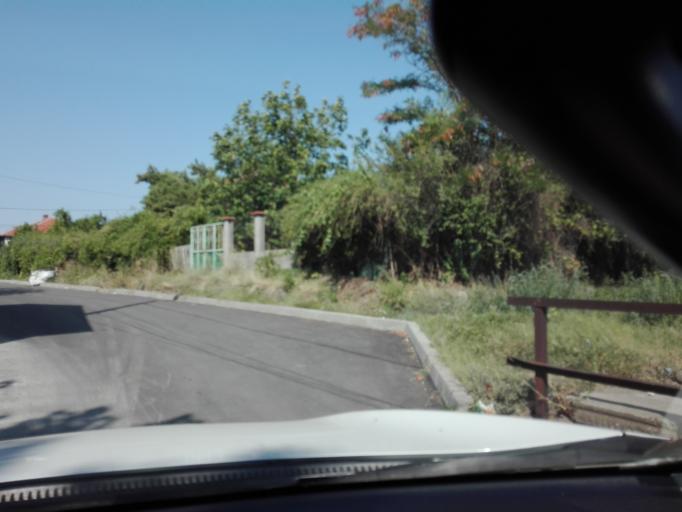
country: BG
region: Burgas
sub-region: Obshtina Kameno
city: Kameno
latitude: 42.6289
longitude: 27.3943
